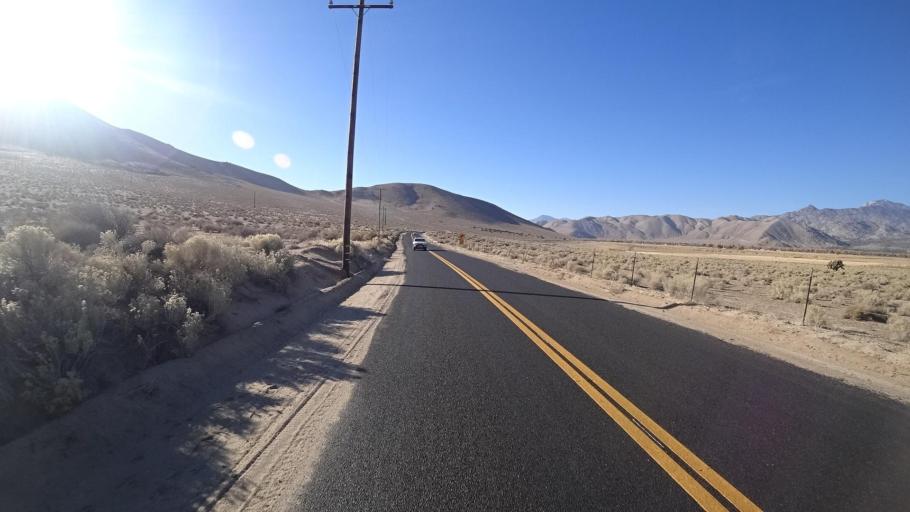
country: US
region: California
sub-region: Kern County
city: Weldon
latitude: 35.6526
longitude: -118.2783
